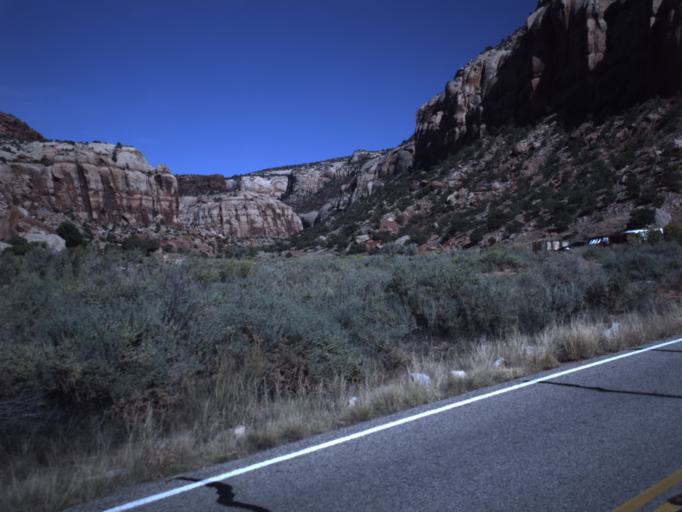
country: US
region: Utah
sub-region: San Juan County
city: Monticello
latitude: 38.0373
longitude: -109.5488
